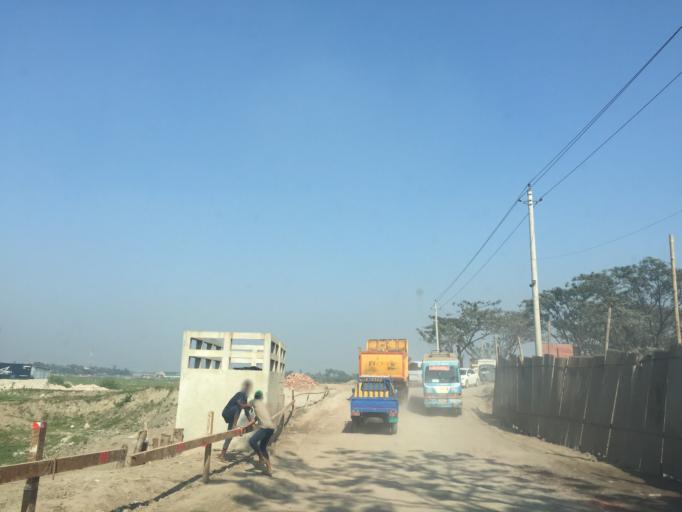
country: BD
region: Dhaka
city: Tungi
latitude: 23.8373
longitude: 90.3400
